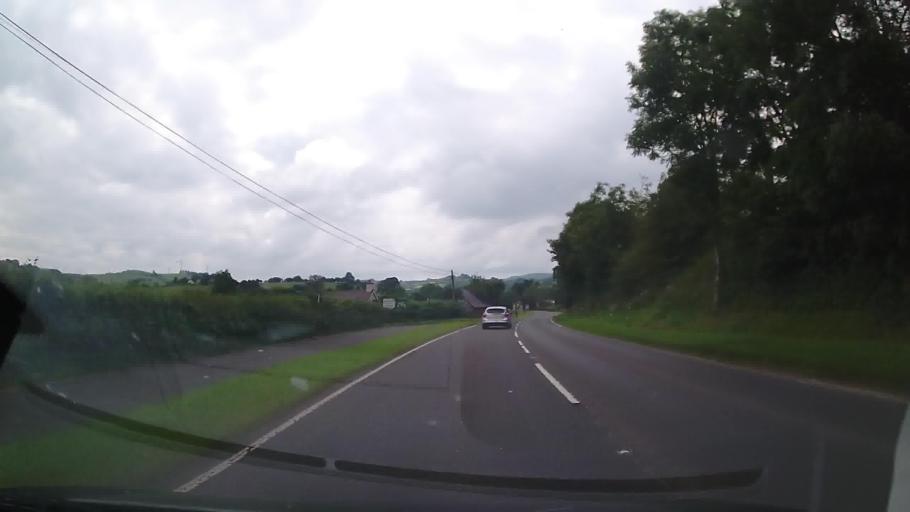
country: GB
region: Wales
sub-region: Denbighshire
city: Llandrillo
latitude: 52.9718
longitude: -3.4453
